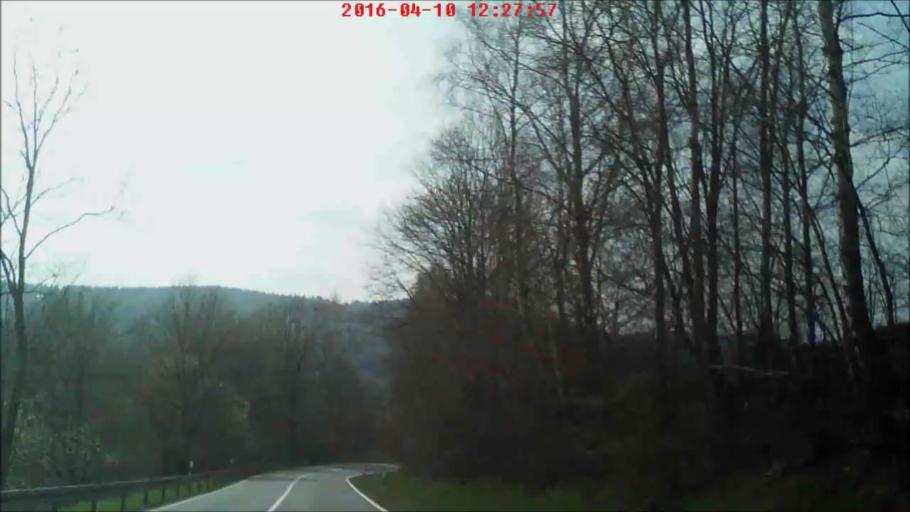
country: DE
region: Thuringia
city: Springstille
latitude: 50.6862
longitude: 10.5397
